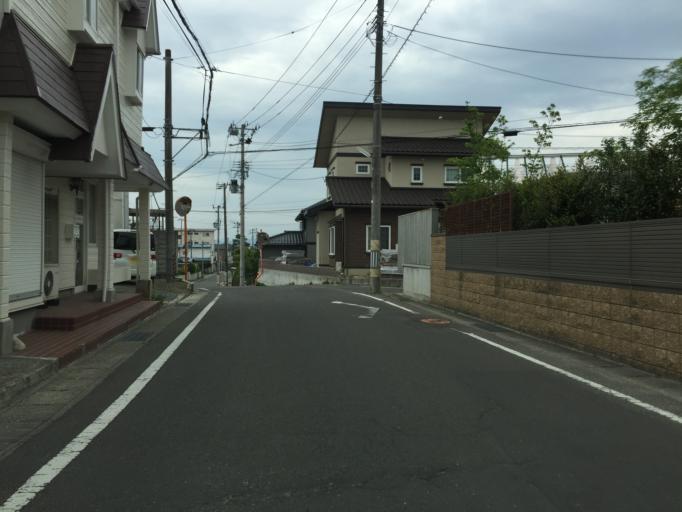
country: JP
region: Fukushima
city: Fukushima-shi
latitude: 37.7883
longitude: 140.4358
